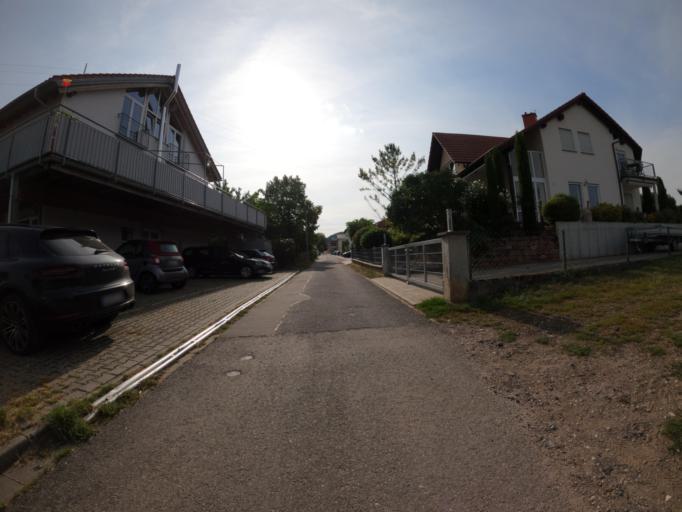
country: DE
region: Rheinland-Pfalz
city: Weisenheim am Berg
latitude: 49.5148
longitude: 8.1607
